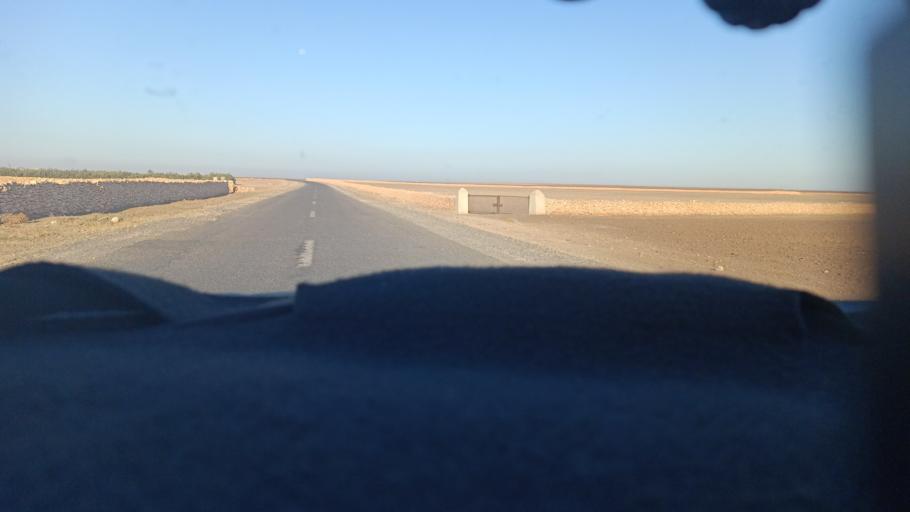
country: MA
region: Doukkala-Abda
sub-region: Safi
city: Youssoufia
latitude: 32.3718
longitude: -8.6953
